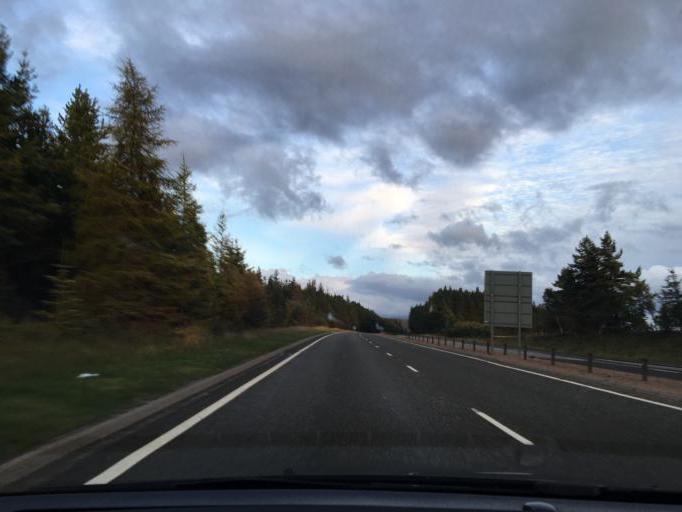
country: GB
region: Scotland
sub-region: Highland
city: Aviemore
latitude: 57.3412
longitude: -3.9927
